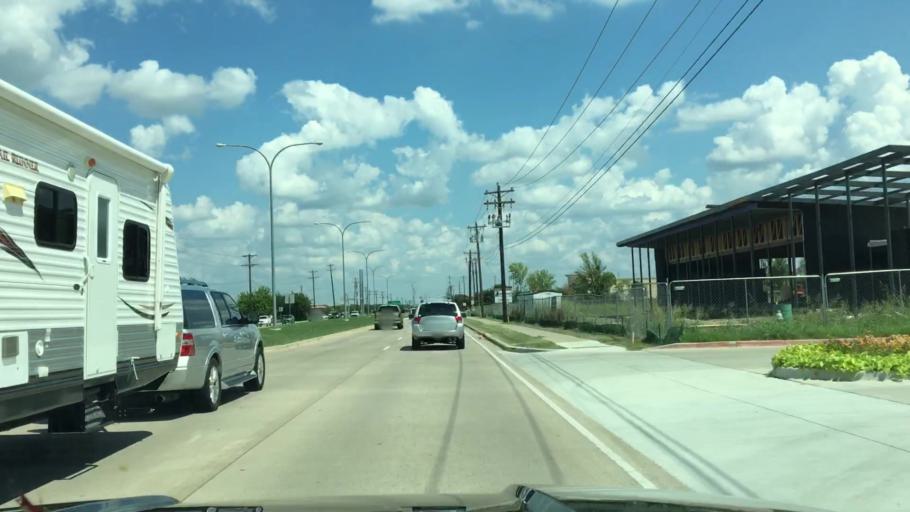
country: US
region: Texas
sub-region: Tarrant County
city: Keller
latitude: 32.9314
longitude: -97.2929
